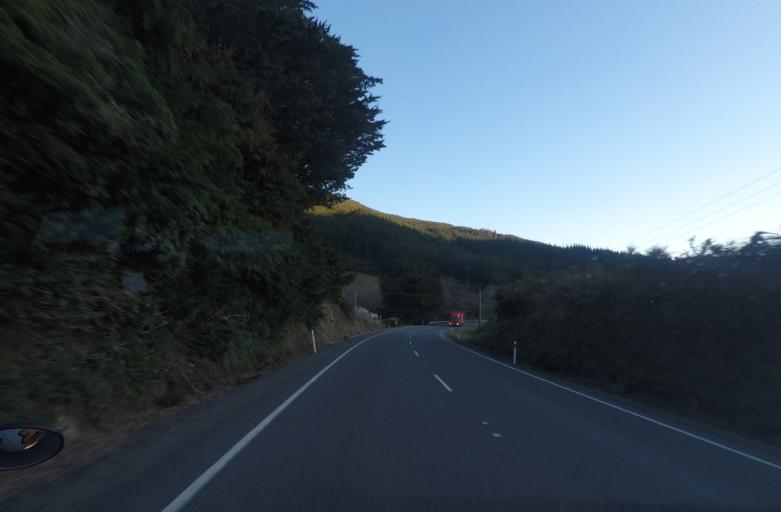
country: NZ
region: Marlborough
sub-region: Marlborough District
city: Picton
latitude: -41.2818
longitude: 173.7268
